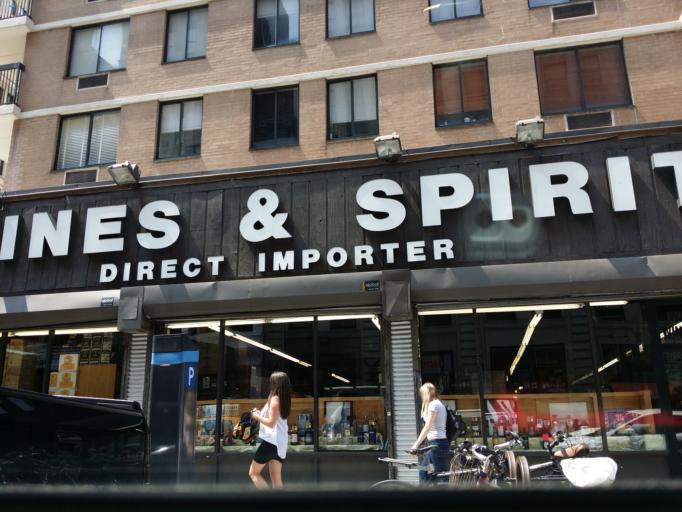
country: US
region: New York
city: New York City
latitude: 40.7301
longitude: -73.9931
